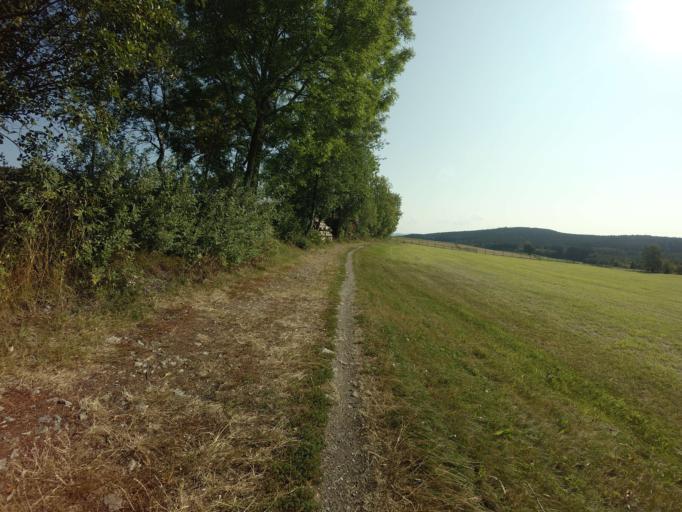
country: AT
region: Upper Austria
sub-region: Politischer Bezirk Urfahr-Umgebung
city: Bad Leonfelden
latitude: 48.5432
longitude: 14.3164
